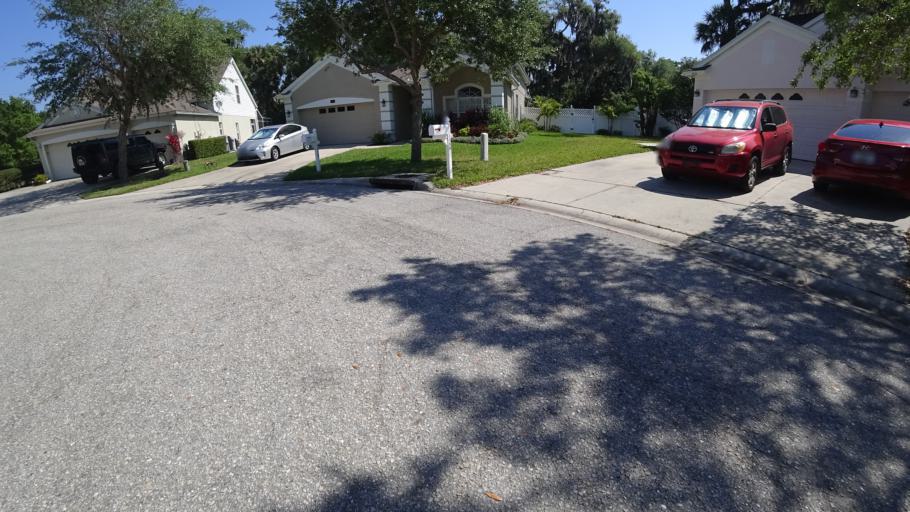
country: US
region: Florida
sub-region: Manatee County
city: Samoset
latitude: 27.4649
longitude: -82.5202
